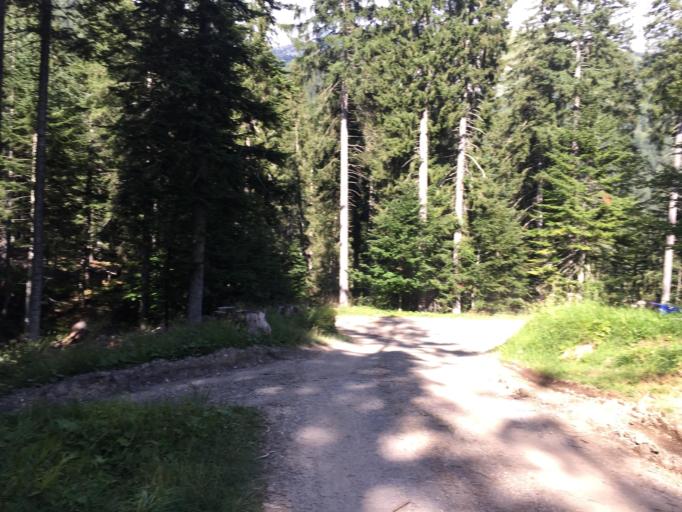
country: IT
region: Friuli Venezia Giulia
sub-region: Provincia di Udine
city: Forni Avoltri
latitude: 46.5939
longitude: 12.7938
